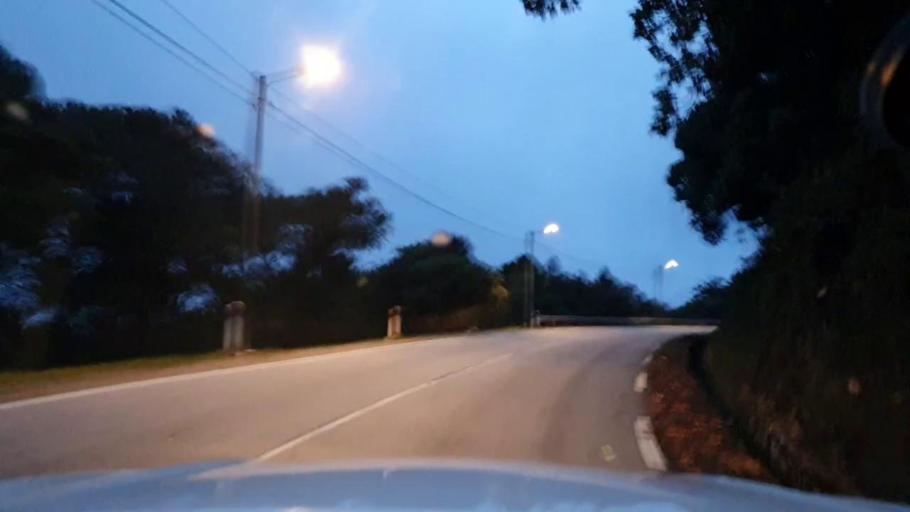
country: RW
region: Southern Province
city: Nzega
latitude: -2.5255
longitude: 29.3780
